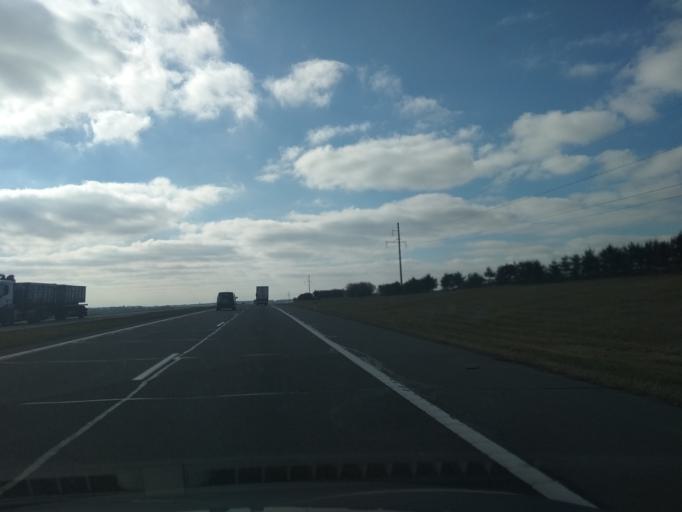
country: BY
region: Minsk
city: Novy Svyerzhan'
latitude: 53.4675
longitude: 26.6149
